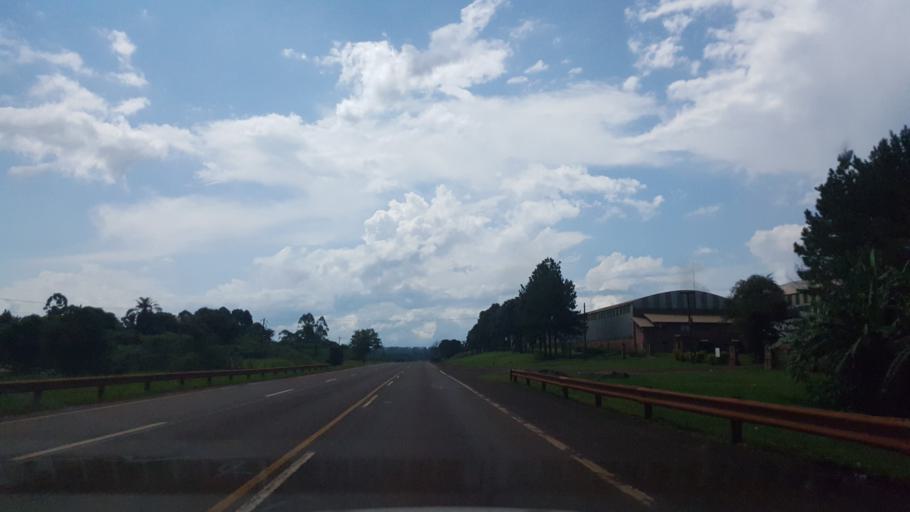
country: AR
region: Misiones
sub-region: Departamento de Eldorado
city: Eldorado
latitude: -26.3188
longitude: -54.6155
